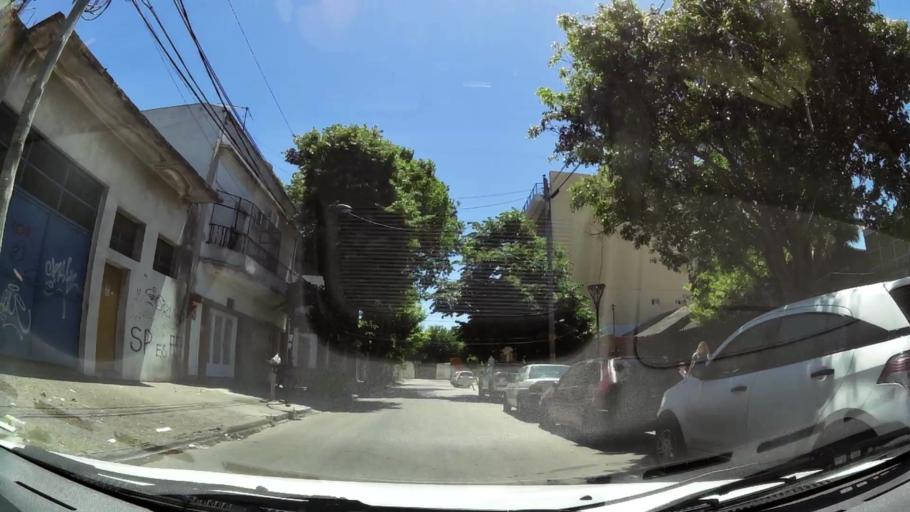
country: AR
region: Buenos Aires
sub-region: Partido de General San Martin
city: General San Martin
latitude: -34.5963
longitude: -58.5342
